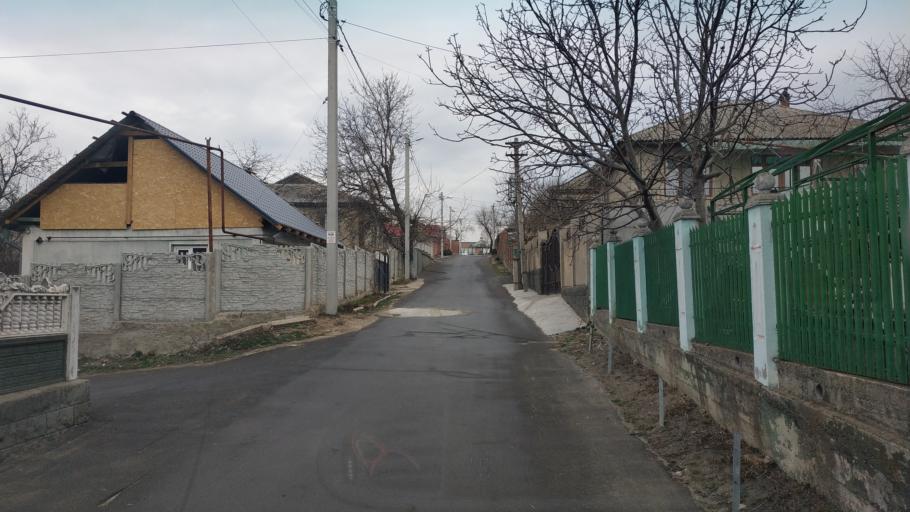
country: MD
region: Chisinau
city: Singera
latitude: 46.9192
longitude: 28.9610
